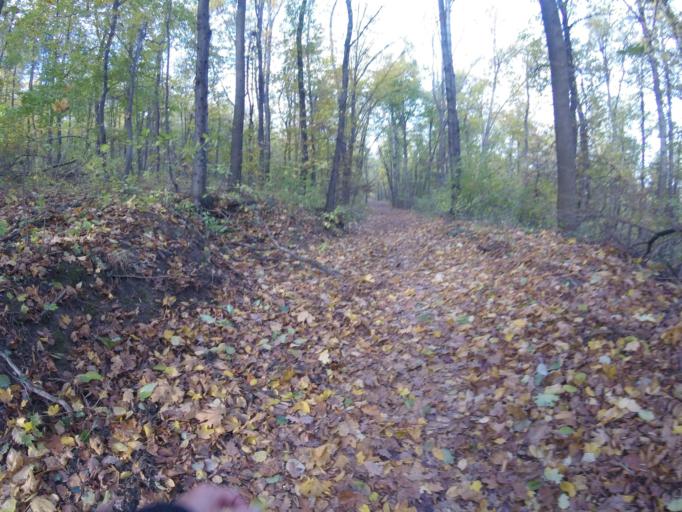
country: HU
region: Pest
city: Budakeszi
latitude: 47.5234
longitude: 18.9560
